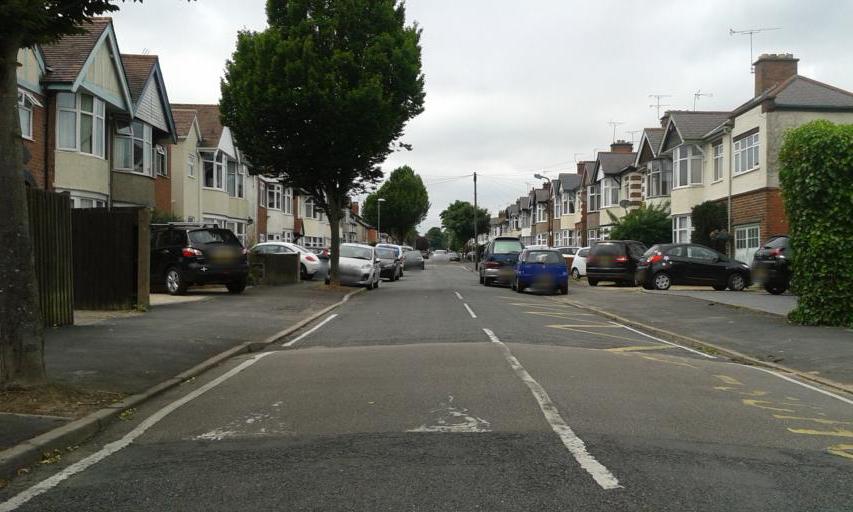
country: GB
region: England
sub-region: Leicestershire
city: Hinckley
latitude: 52.5425
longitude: -1.3539
